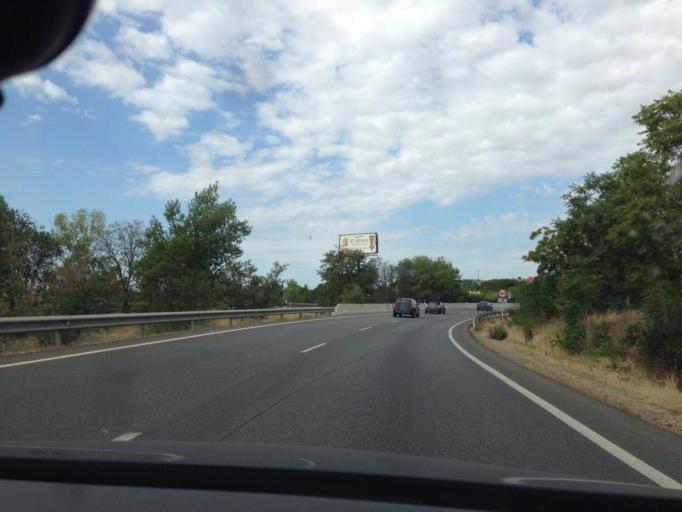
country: ES
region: Madrid
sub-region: Provincia de Madrid
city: San Sebastian de los Reyes
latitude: 40.5831
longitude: -3.5701
